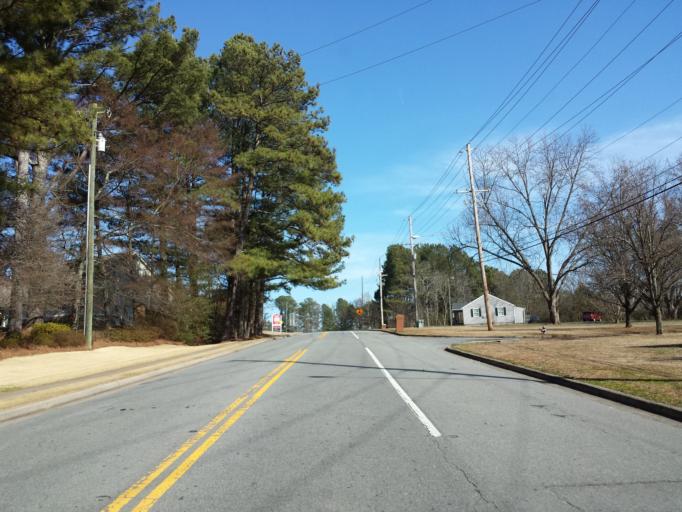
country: US
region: Georgia
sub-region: Cobb County
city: Kennesaw
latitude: 34.0289
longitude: -84.5931
